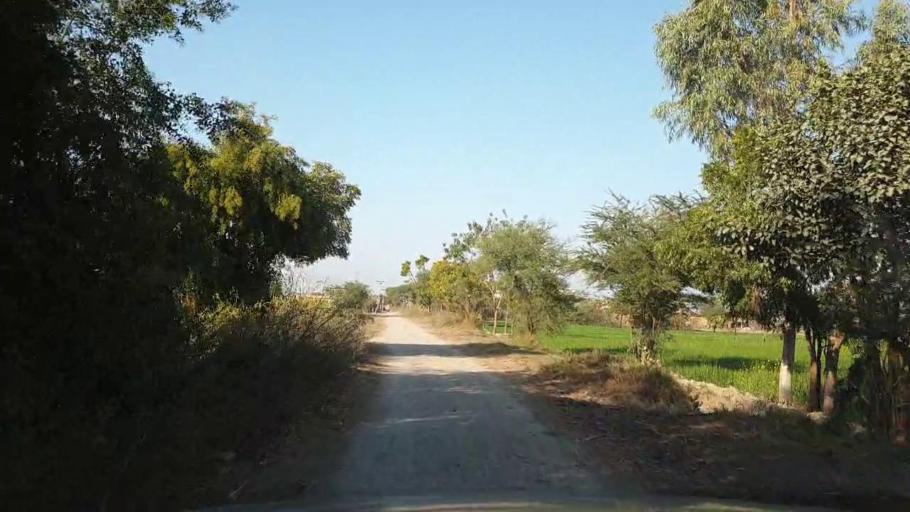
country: PK
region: Sindh
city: Tando Allahyar
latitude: 25.5133
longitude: 68.6561
